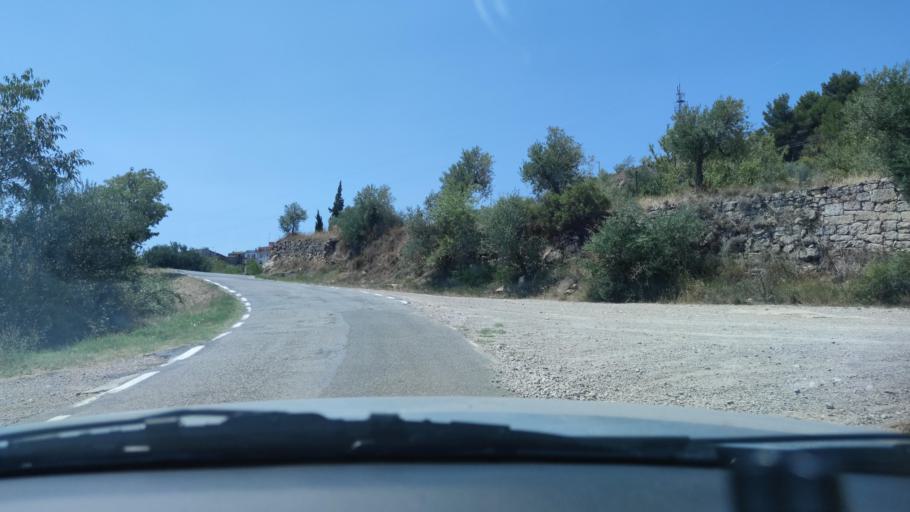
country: ES
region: Catalonia
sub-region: Provincia de Lleida
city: Fulleda
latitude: 41.4664
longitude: 1.0250
